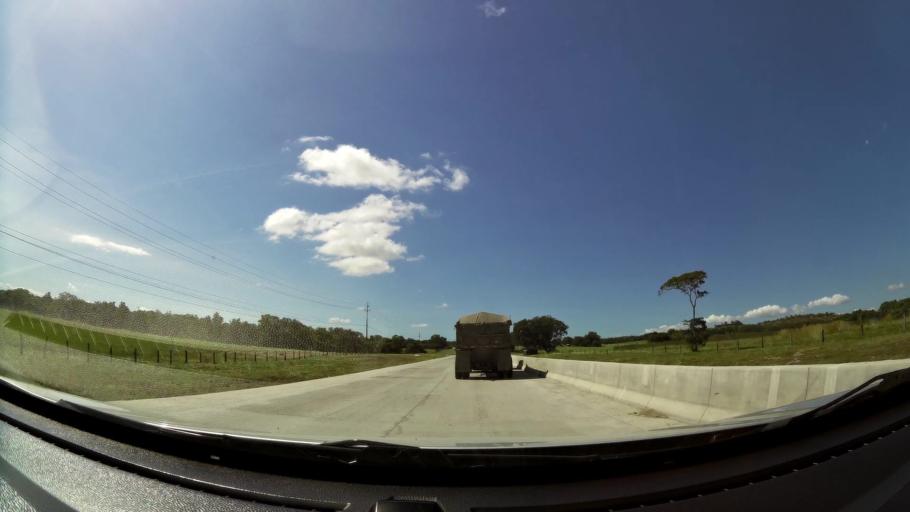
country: CR
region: Guanacaste
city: Bagaces
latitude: 10.5404
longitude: -85.3138
